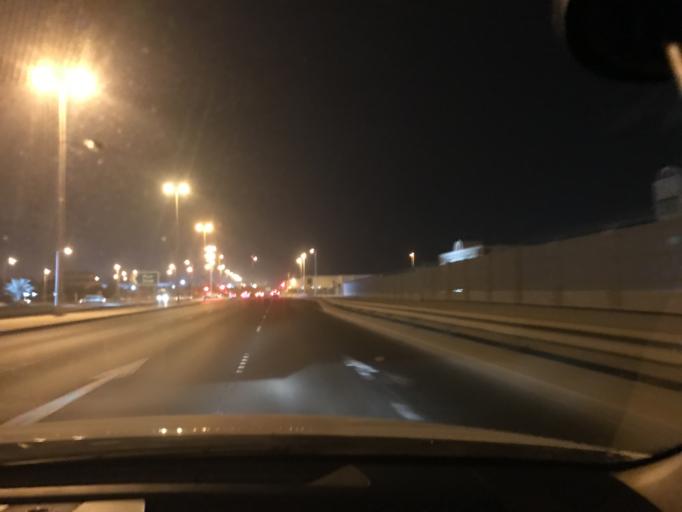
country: BH
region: Muharraq
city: Al Hadd
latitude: 26.2611
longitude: 50.6426
